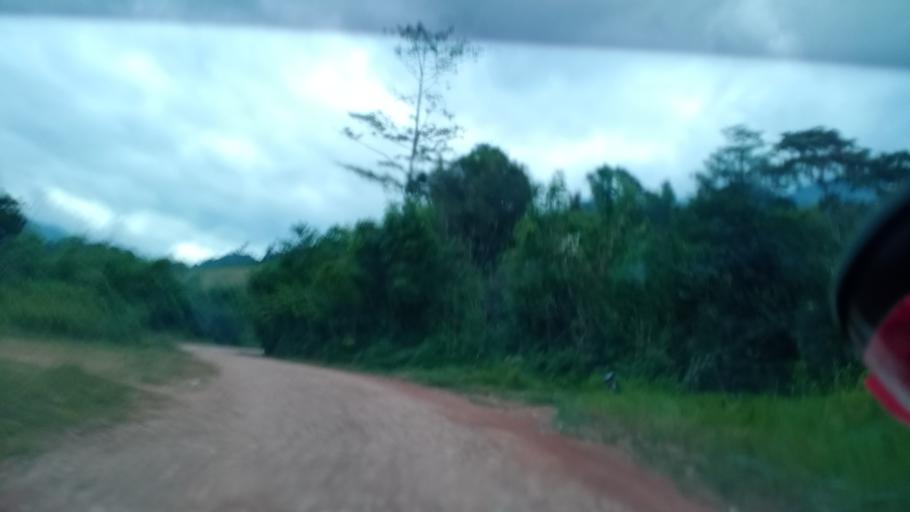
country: TH
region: Changwat Bueng Kan
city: Pak Khat
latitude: 18.7146
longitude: 103.2187
